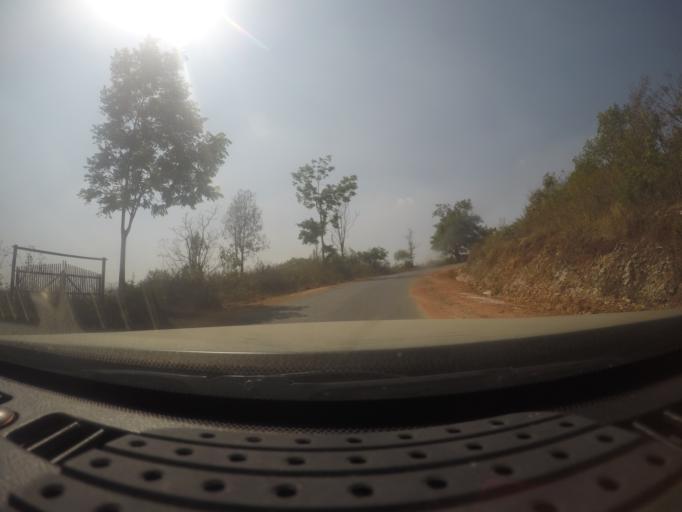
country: MM
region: Shan
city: Taunggyi
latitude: 21.0752
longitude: 96.4978
